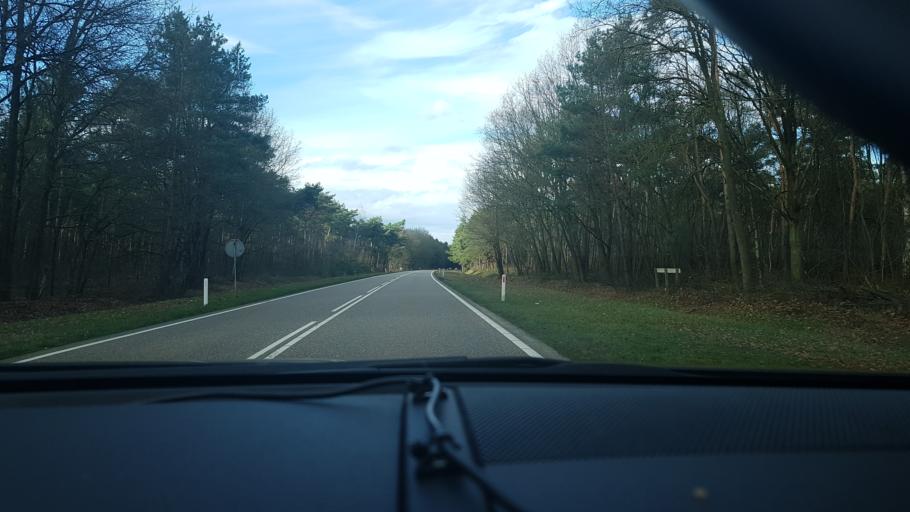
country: NL
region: Limburg
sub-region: Gemeente Peel en Maas
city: Maasbree
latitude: 51.3161
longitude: 6.0487
